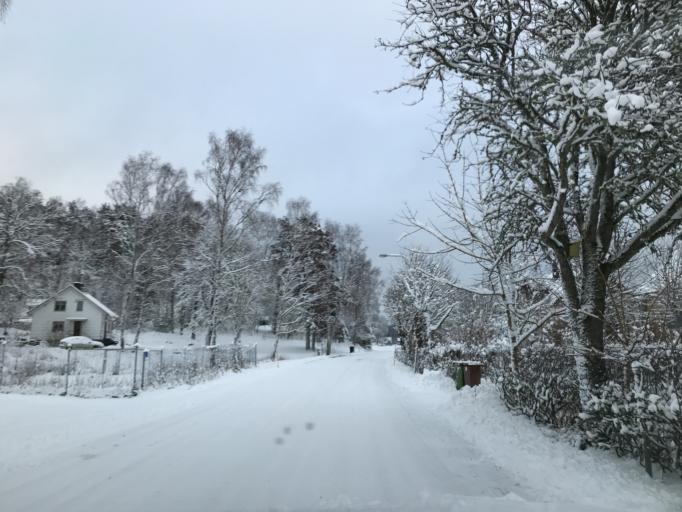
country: SE
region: Vaestra Goetaland
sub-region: Bollebygds Kommun
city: Bollebygd
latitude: 57.7954
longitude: 12.6359
